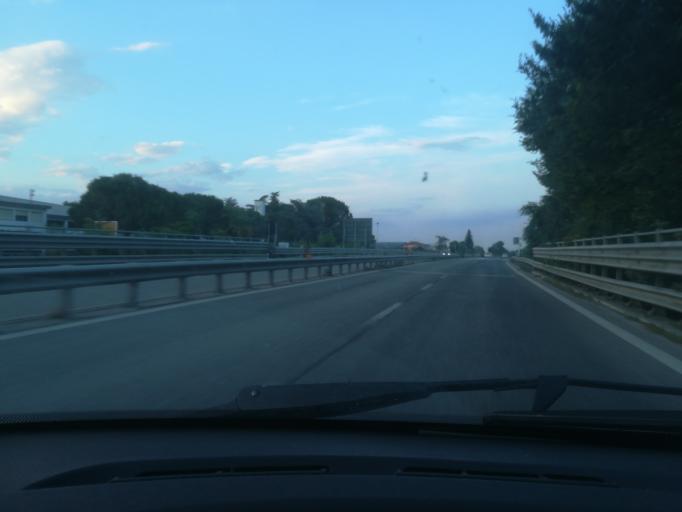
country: IT
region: The Marches
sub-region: Provincia di Macerata
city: Pollenza
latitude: 43.2292
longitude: 13.3462
